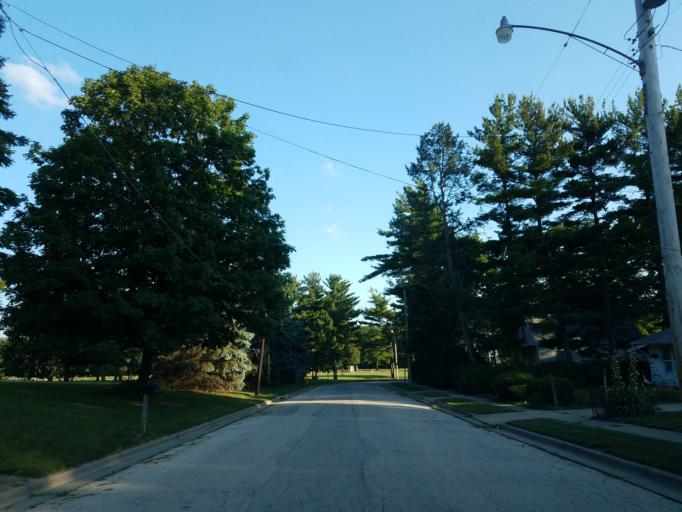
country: US
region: Illinois
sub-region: McLean County
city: Bloomington
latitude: 40.4669
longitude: -89.0097
